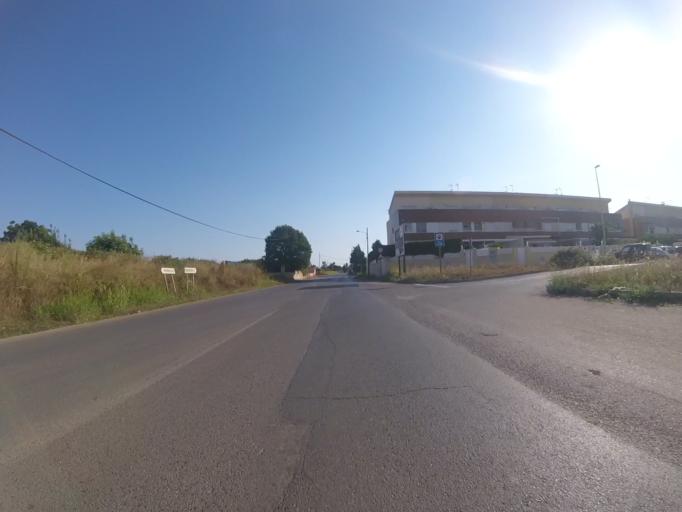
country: ES
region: Valencia
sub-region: Provincia de Castello
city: Benicarlo
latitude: 40.4056
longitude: 0.4162
